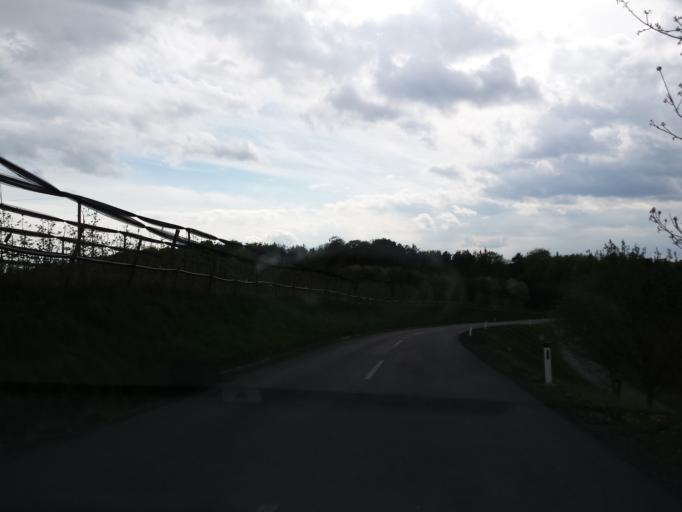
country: AT
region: Styria
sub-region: Politischer Bezirk Suedoststeiermark
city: Hatzendorf
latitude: 46.9879
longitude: 16.0087
